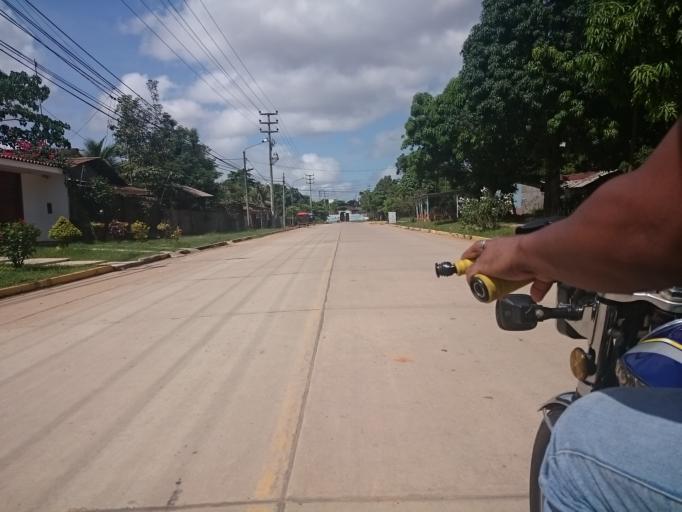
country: PE
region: Ucayali
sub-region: Provincia de Coronel Portillo
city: Pucallpa
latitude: -8.3697
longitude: -74.5621
